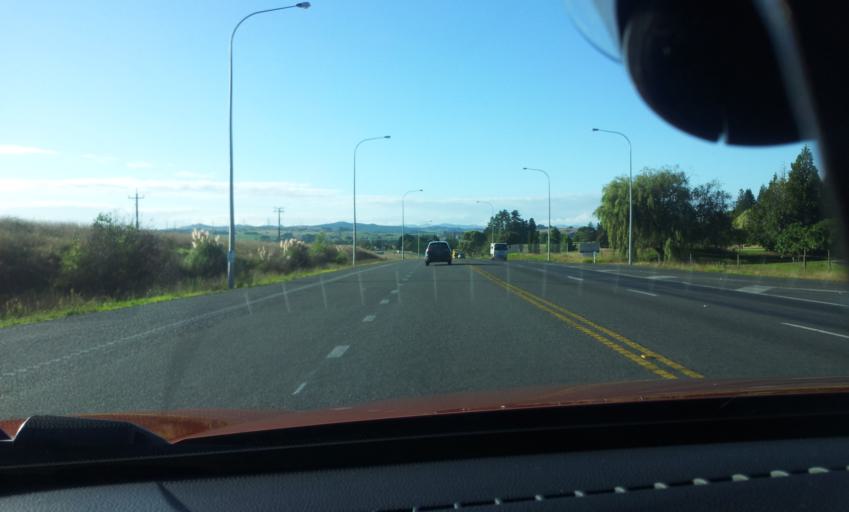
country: NZ
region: Waikato
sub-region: Waikato District
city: Te Kauwhata
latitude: -37.2314
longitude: 175.1633
